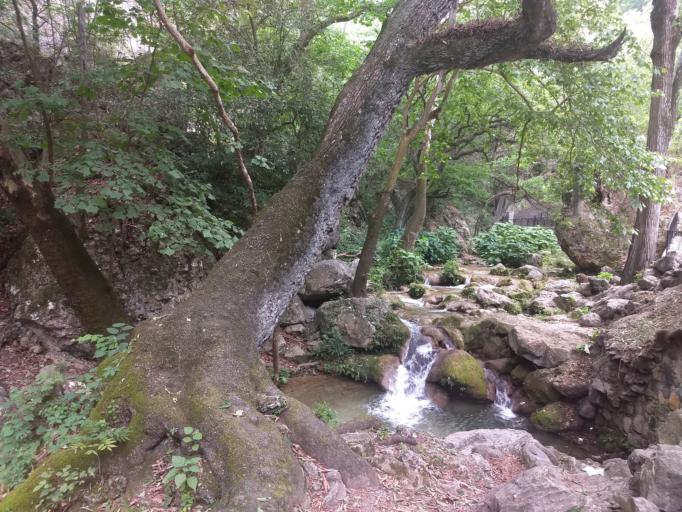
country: MX
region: Nuevo Leon
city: Santiago
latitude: 25.3634
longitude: -100.1637
